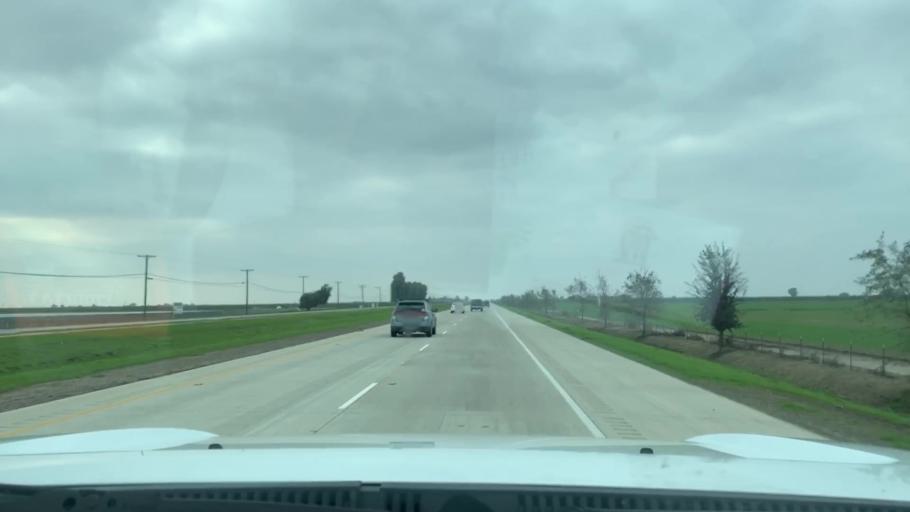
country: US
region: California
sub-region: Kings County
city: Home Garden
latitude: 36.3287
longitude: -119.5349
